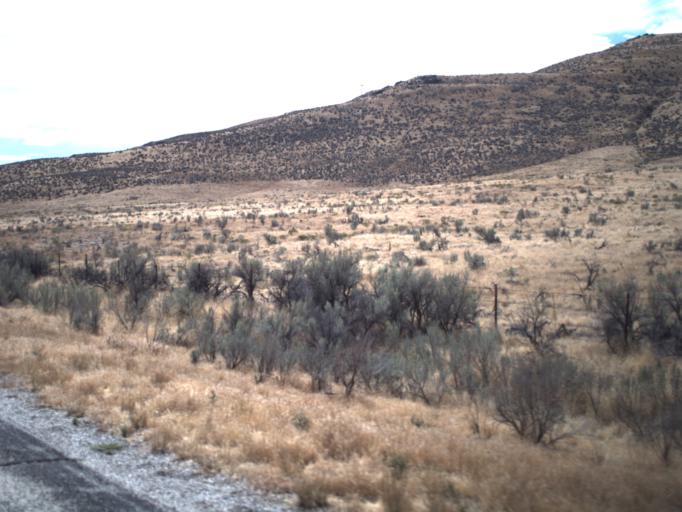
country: US
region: Utah
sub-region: Box Elder County
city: Tremonton
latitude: 41.7031
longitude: -112.4486
